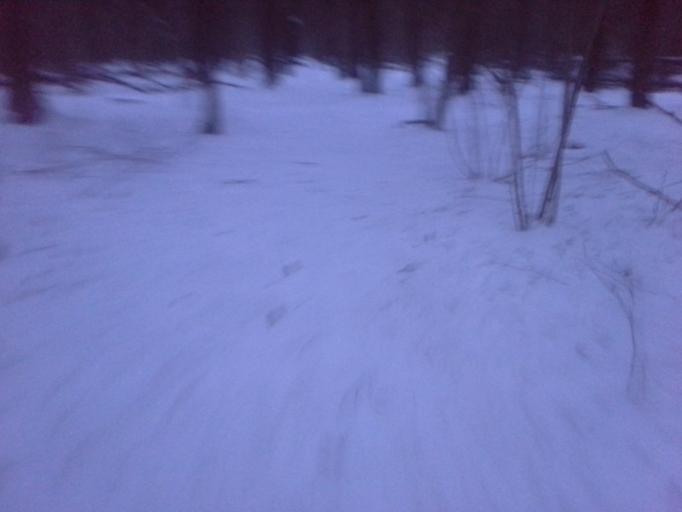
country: RU
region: Moscow
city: Yasenevo
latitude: 55.5653
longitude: 37.5490
